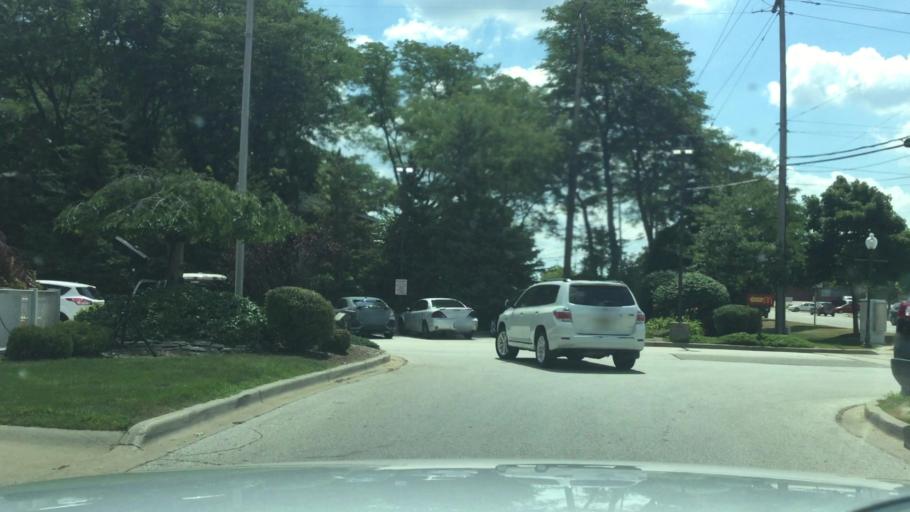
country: US
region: Michigan
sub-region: Genesee County
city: Grand Blanc
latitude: 42.9213
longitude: -83.6218
